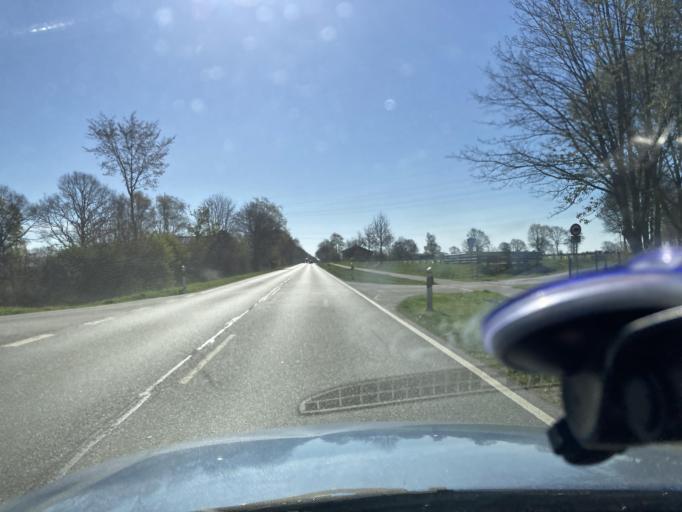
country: DE
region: Schleswig-Holstein
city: Ostrohe
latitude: 54.1894
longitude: 9.1600
